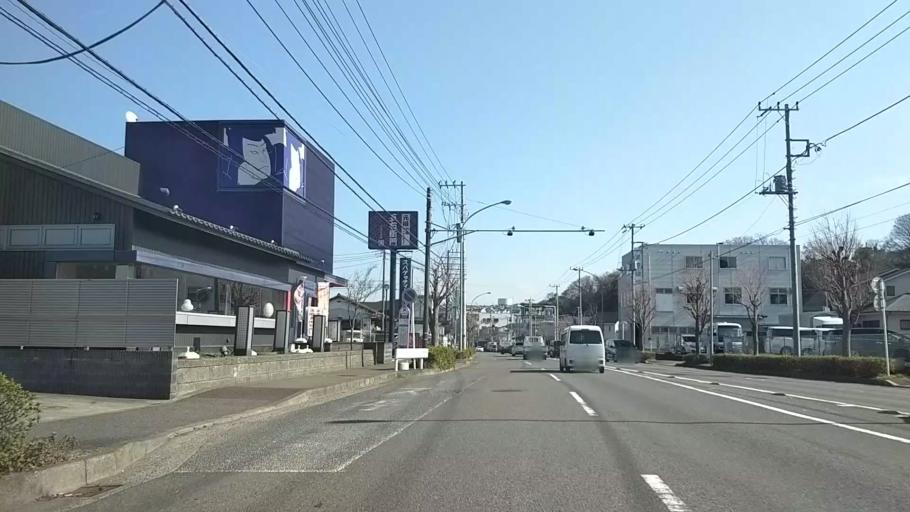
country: JP
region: Kanagawa
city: Zushi
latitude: 35.3646
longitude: 139.6101
